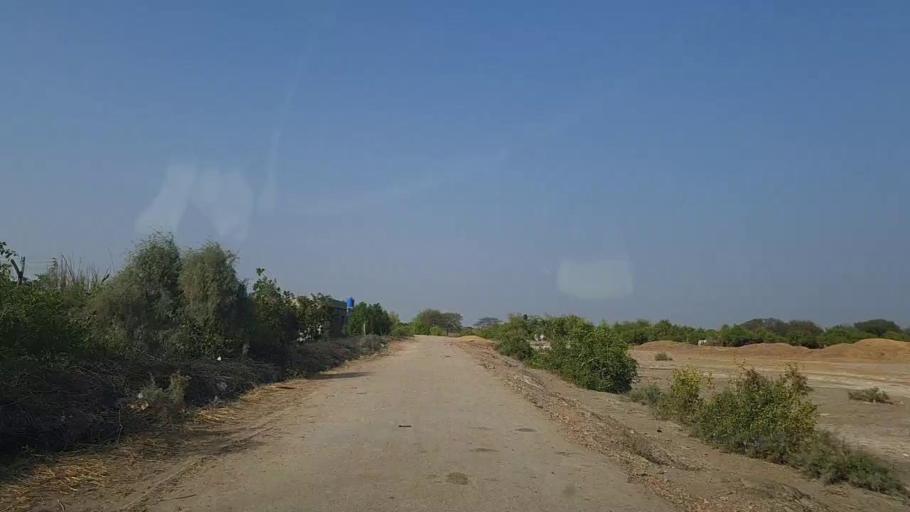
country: PK
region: Sindh
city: Mirpur Sakro
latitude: 24.5695
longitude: 67.6857
